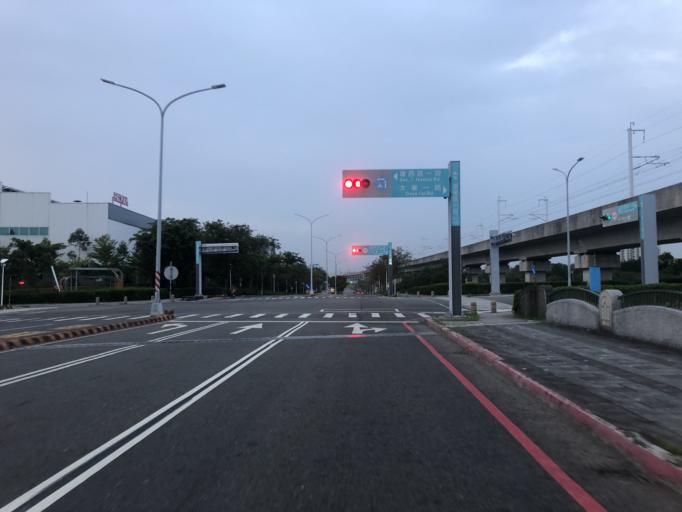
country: TW
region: Taiwan
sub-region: Tainan
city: Tainan
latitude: 23.0905
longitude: 120.2863
